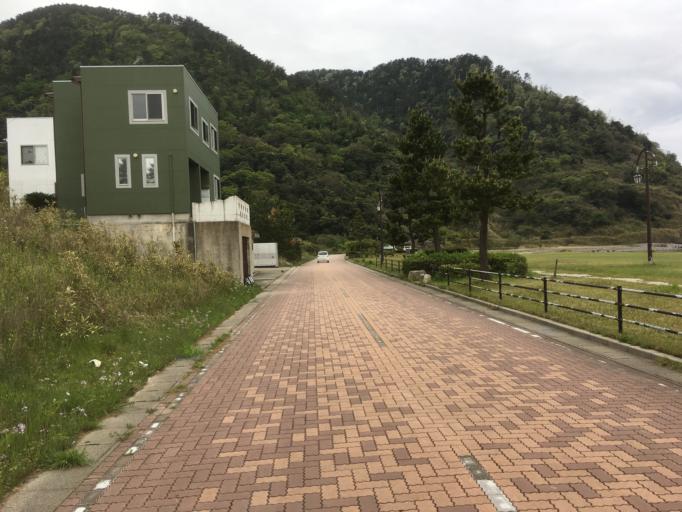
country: JP
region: Tottori
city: Tottori
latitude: 35.5742
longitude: 134.2905
